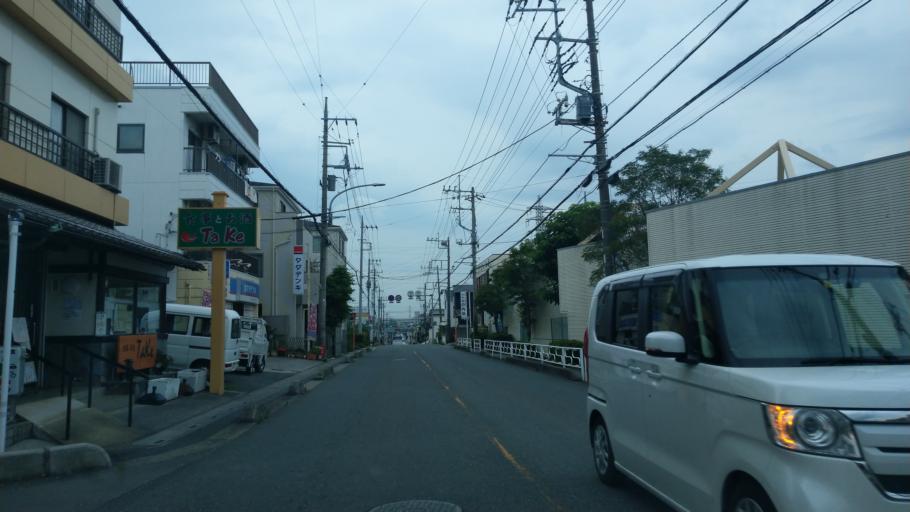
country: JP
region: Saitama
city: Shimotoda
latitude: 35.8568
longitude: 139.6944
